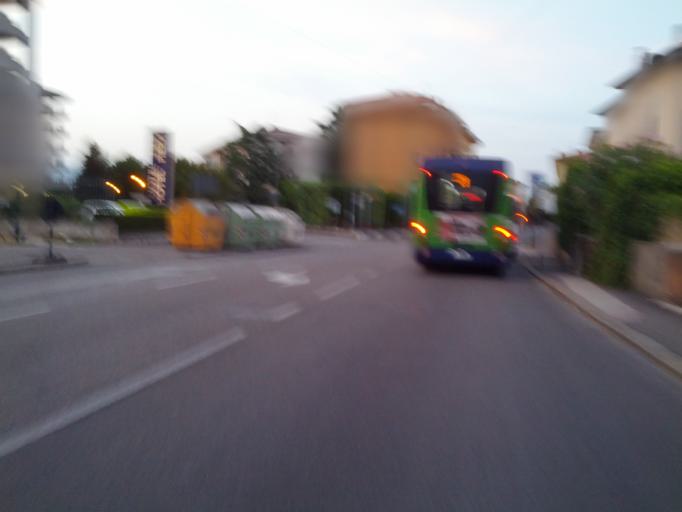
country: IT
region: Veneto
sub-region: Provincia di Verona
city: Verona
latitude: 45.4211
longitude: 10.9772
